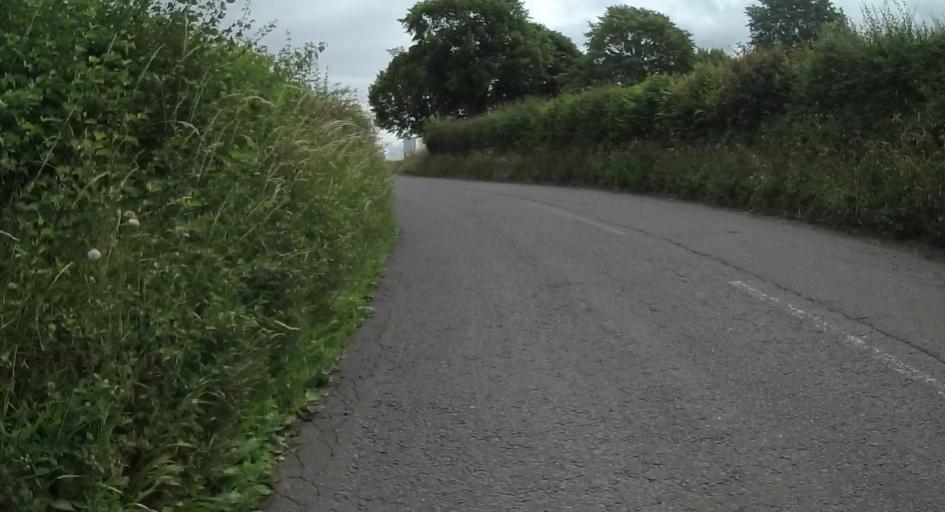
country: GB
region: England
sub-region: Surrey
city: Farnham
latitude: 51.2213
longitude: -0.8471
